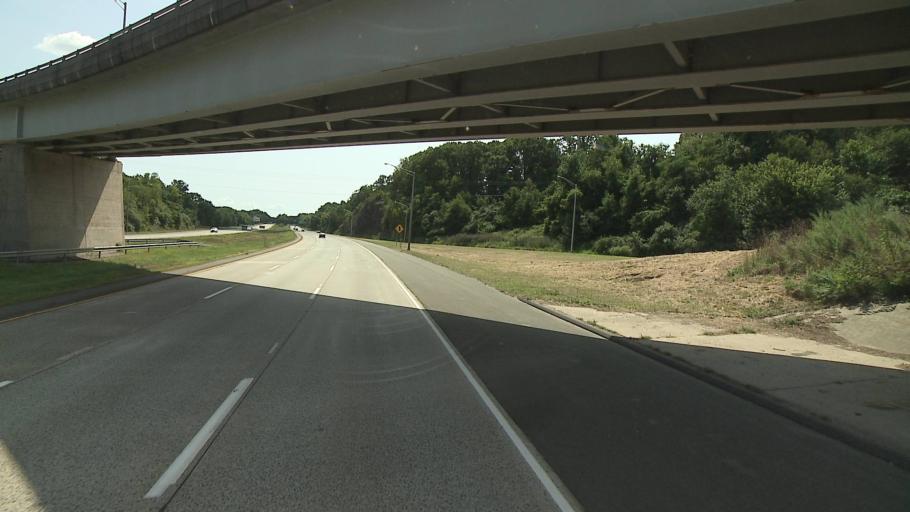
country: US
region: Connecticut
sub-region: Fairfield County
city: Trumbull
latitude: 41.2328
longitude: -73.1899
